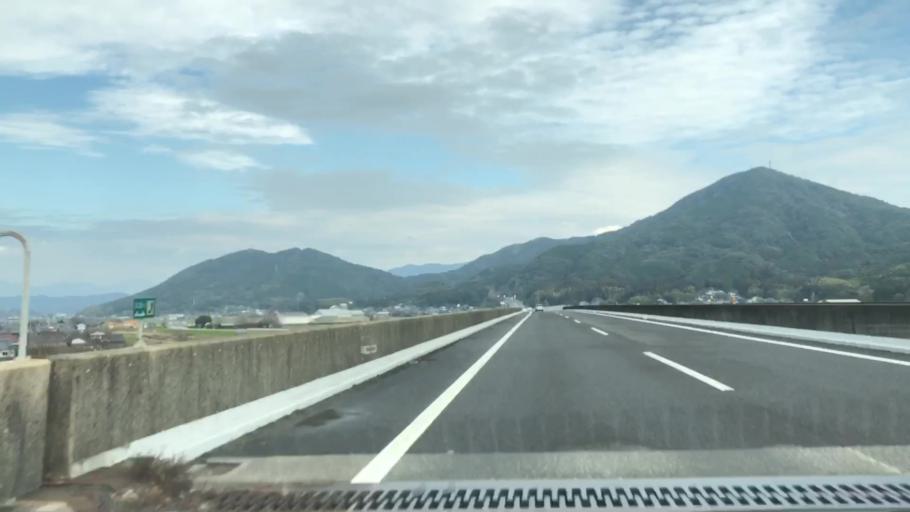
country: JP
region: Saga Prefecture
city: Takeocho-takeo
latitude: 33.1786
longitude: 130.0476
